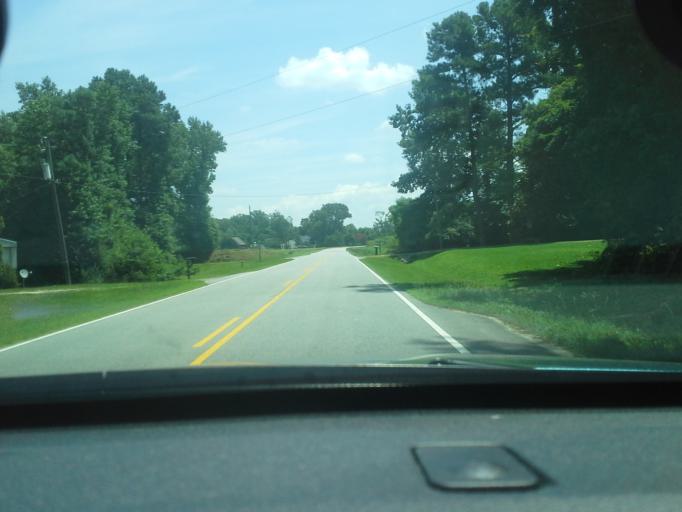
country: US
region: North Carolina
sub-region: Chowan County
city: Edenton
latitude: 35.9297
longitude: -76.6077
